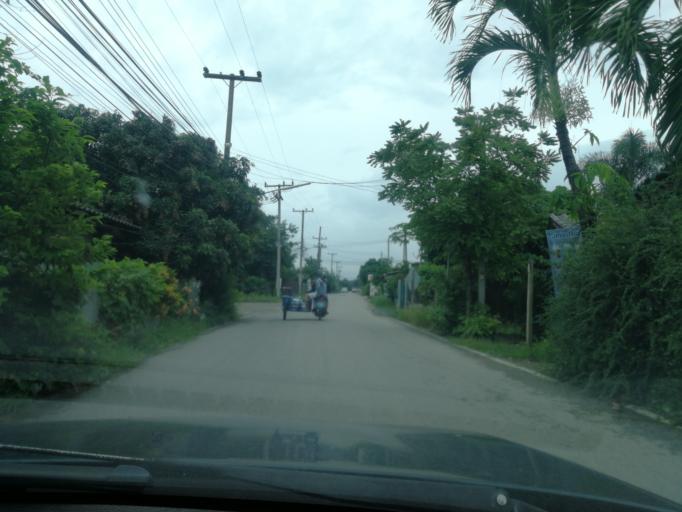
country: TH
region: Chiang Mai
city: San Pa Tong
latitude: 18.6071
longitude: 98.9066
